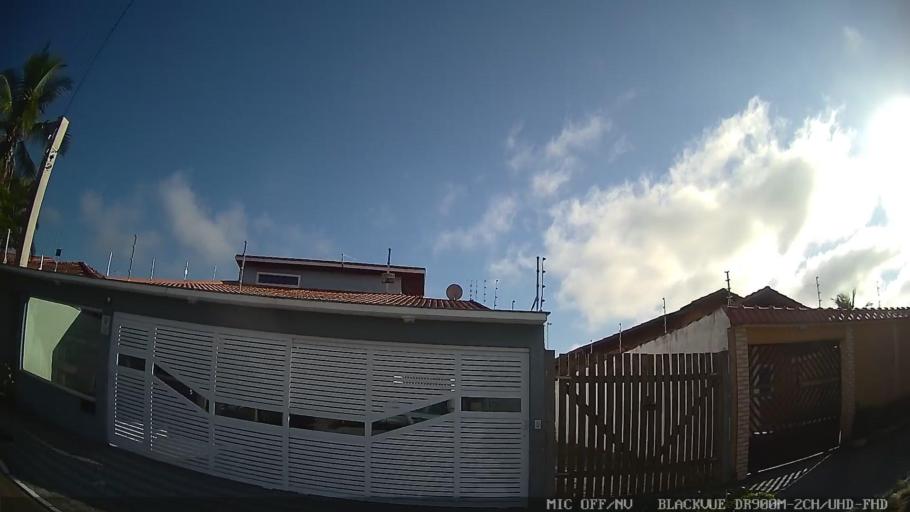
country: BR
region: Sao Paulo
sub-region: Peruibe
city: Peruibe
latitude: -24.3003
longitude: -46.9806
